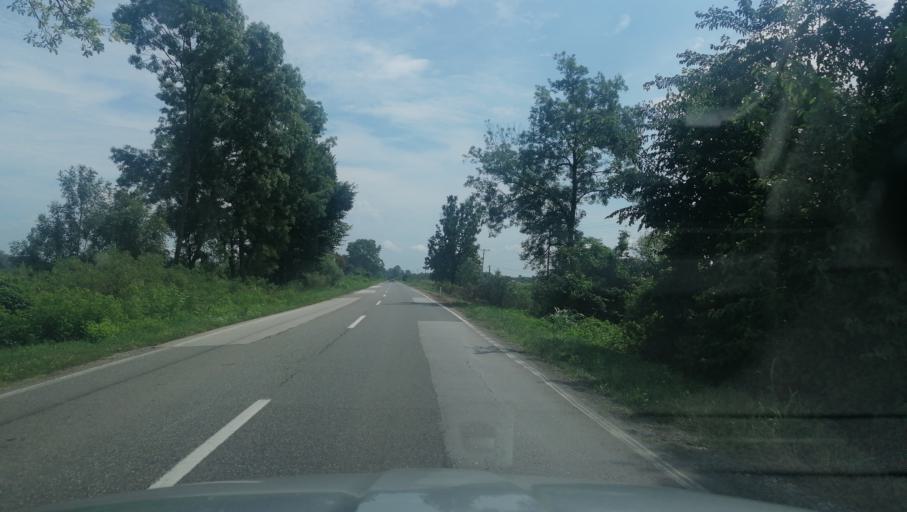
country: BA
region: Republika Srpska
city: Bosanski Samac
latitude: 45.0414
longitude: 18.4943
